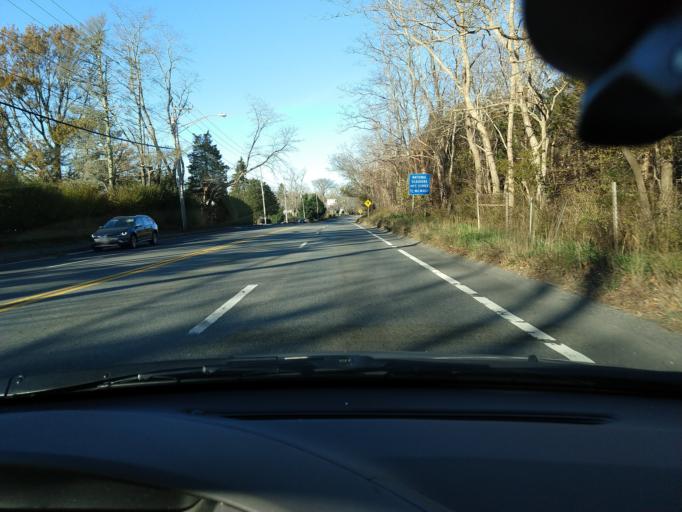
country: US
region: Massachusetts
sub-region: Barnstable County
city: Eastham
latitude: 41.8320
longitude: -69.9738
